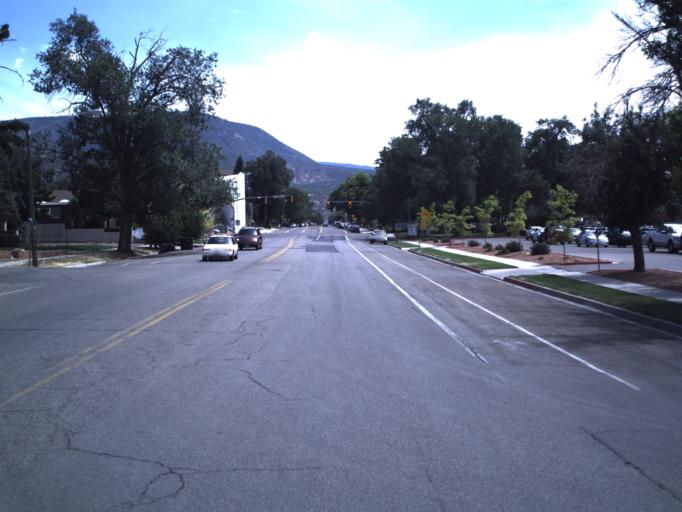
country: US
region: Utah
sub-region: Iron County
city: Cedar City
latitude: 37.6789
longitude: -113.0670
